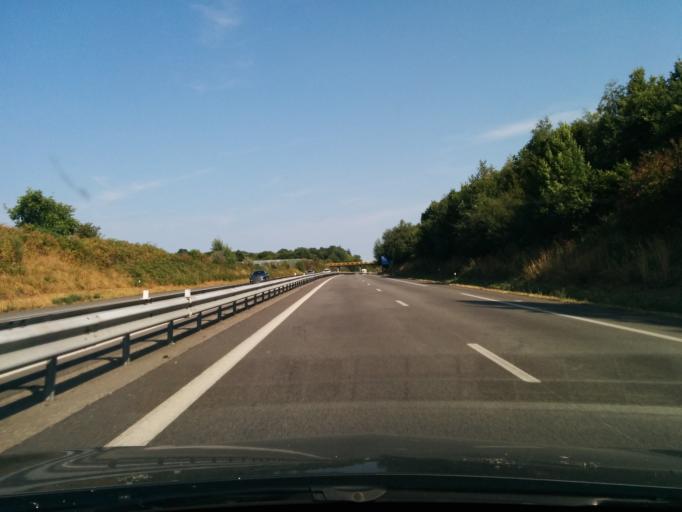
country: FR
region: Limousin
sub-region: Departement de la Haute-Vienne
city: Vicq-sur-Breuilh
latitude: 45.6438
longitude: 1.4132
